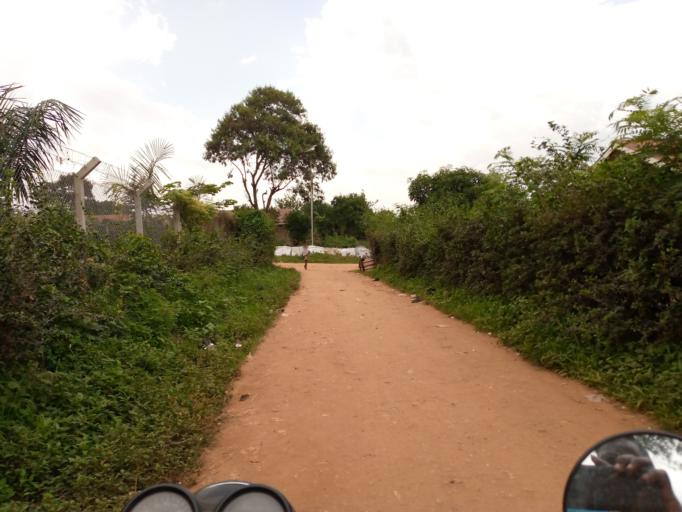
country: UG
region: Eastern Region
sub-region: Mbale District
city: Mbale
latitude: 1.0830
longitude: 34.1696
